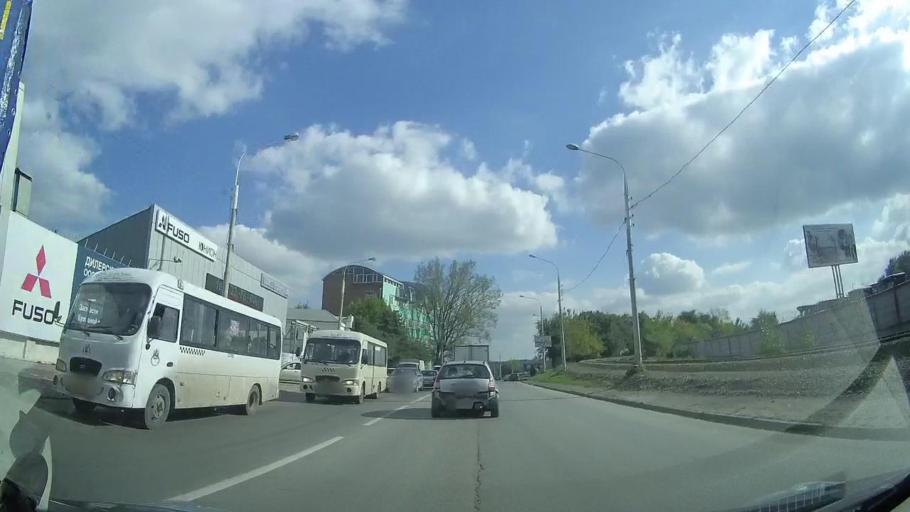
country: RU
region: Rostov
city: Imeni Chkalova
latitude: 47.2635
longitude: 39.7710
